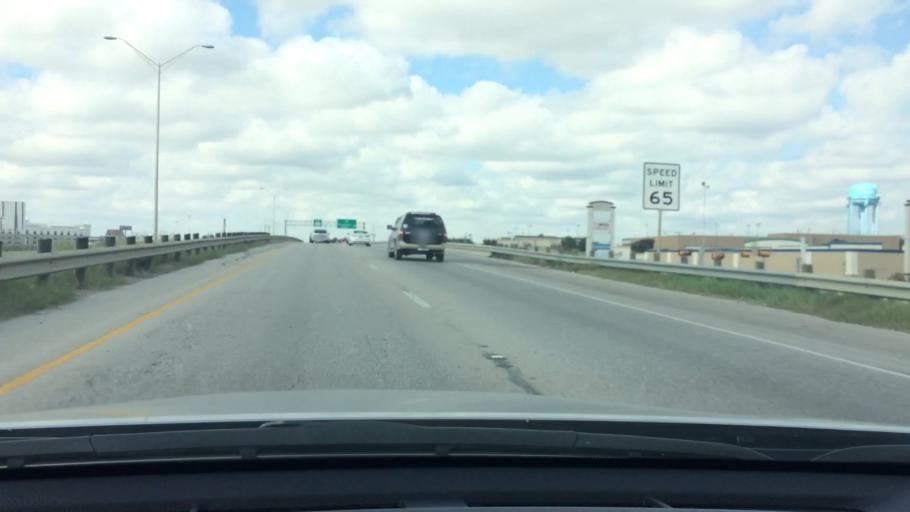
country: US
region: Texas
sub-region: Bexar County
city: Live Oak
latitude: 29.5596
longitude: -98.3264
